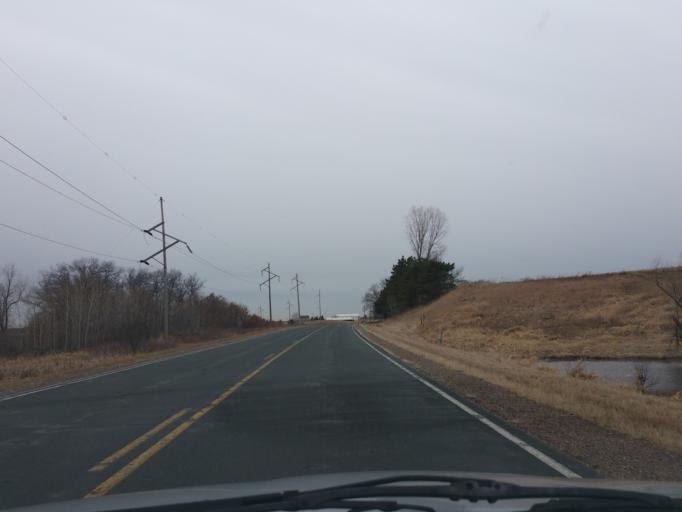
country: US
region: Wisconsin
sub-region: Saint Croix County
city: Roberts
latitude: 45.0360
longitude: -92.5883
